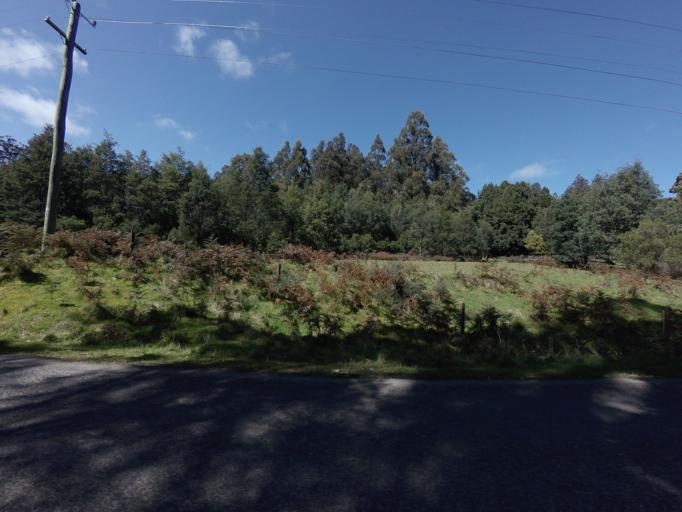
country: AU
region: Tasmania
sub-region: Derwent Valley
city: New Norfolk
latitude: -42.7588
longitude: 146.6156
